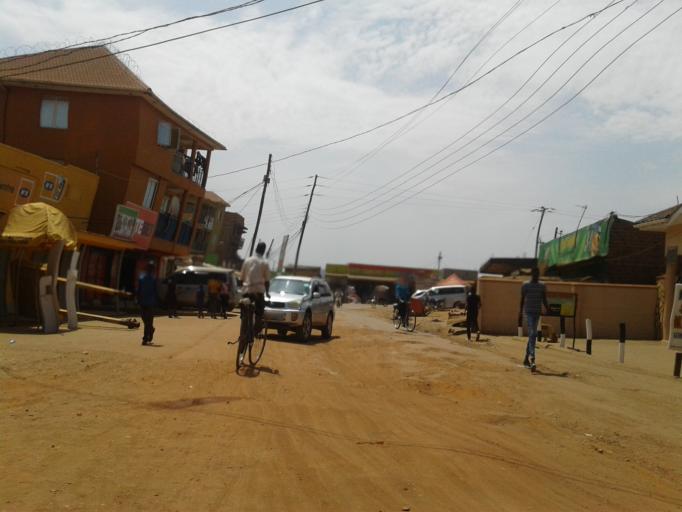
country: UG
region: Central Region
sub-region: Kampala District
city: Kampala
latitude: 0.2569
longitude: 32.6356
